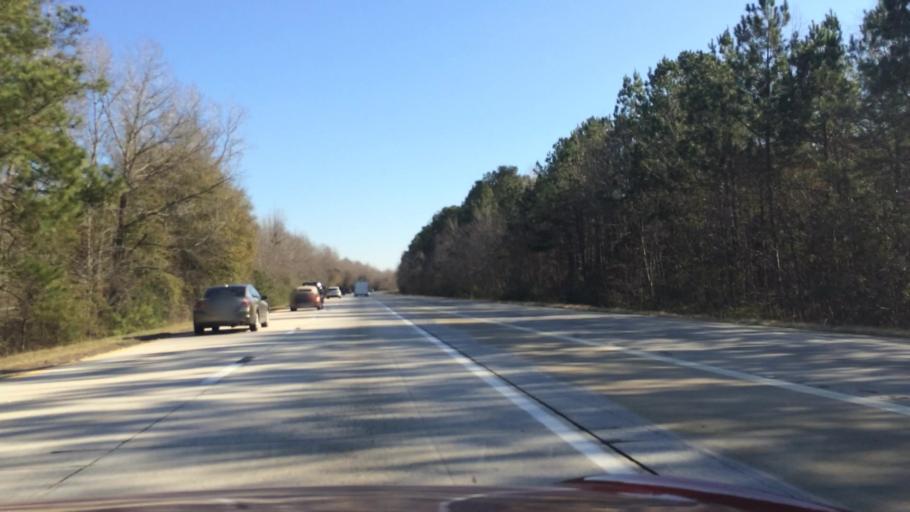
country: US
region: South Carolina
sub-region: Orangeburg County
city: Holly Hill
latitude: 33.2674
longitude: -80.4844
